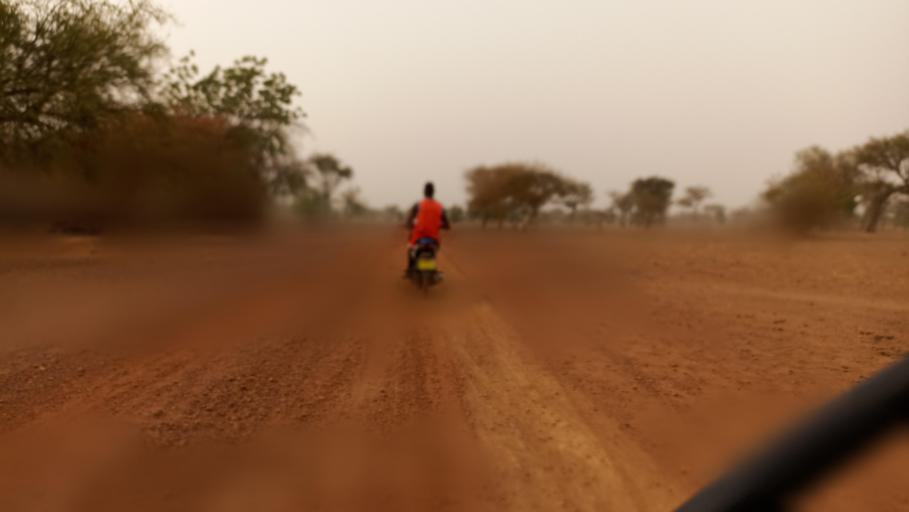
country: BF
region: Nord
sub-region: Province du Zondoma
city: Gourcy
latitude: 13.2417
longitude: -2.5848
